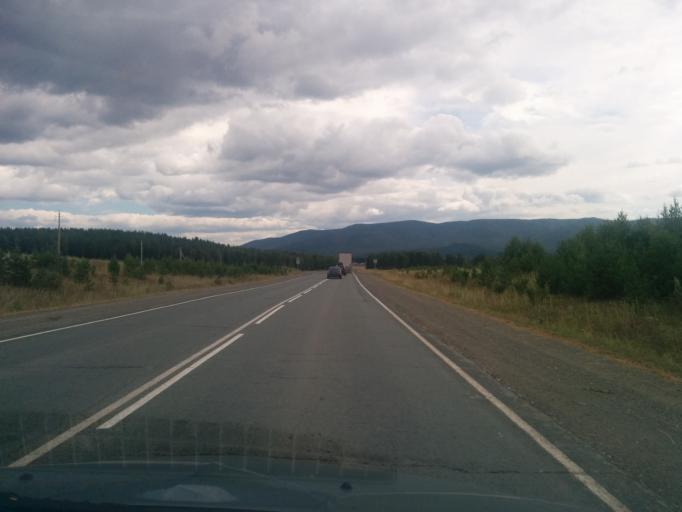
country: RU
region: Bashkortostan
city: Lomovka
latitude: 53.8935
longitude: 58.0932
